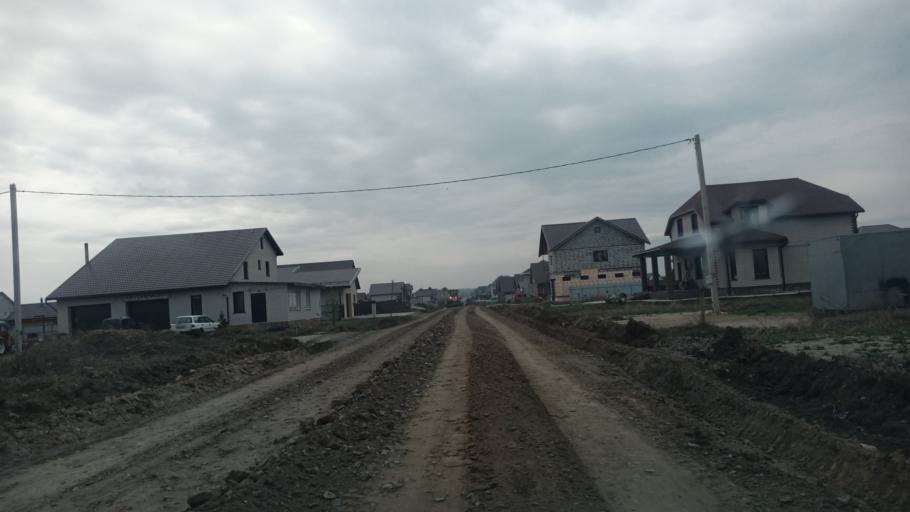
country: RU
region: Altai Krai
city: Yuzhnyy
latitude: 53.2281
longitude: 83.6913
